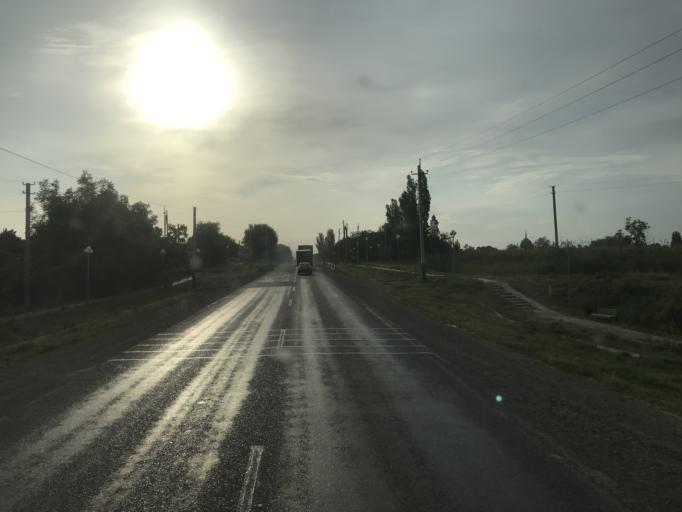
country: UZ
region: Toshkent
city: Salor
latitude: 41.4937
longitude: 69.3120
